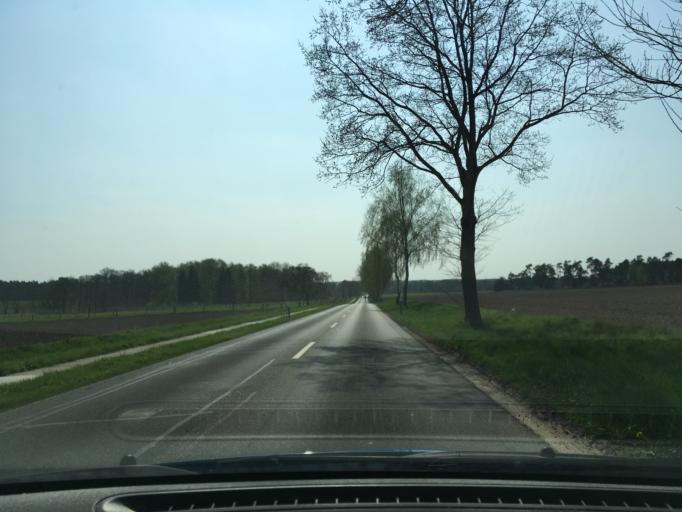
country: DE
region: Lower Saxony
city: Kirchgellersen
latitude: 53.2510
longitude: 10.3147
